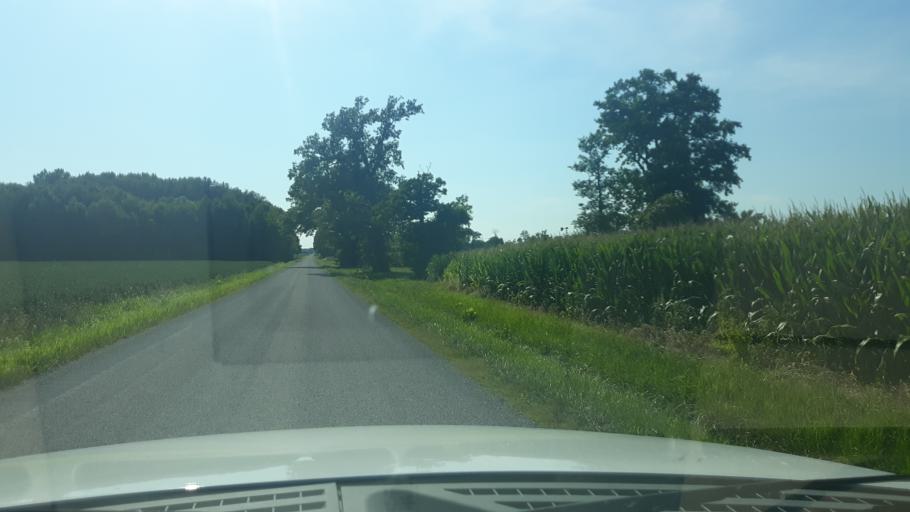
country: US
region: Illinois
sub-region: Saline County
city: Eldorado
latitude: 37.8632
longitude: -88.4870
